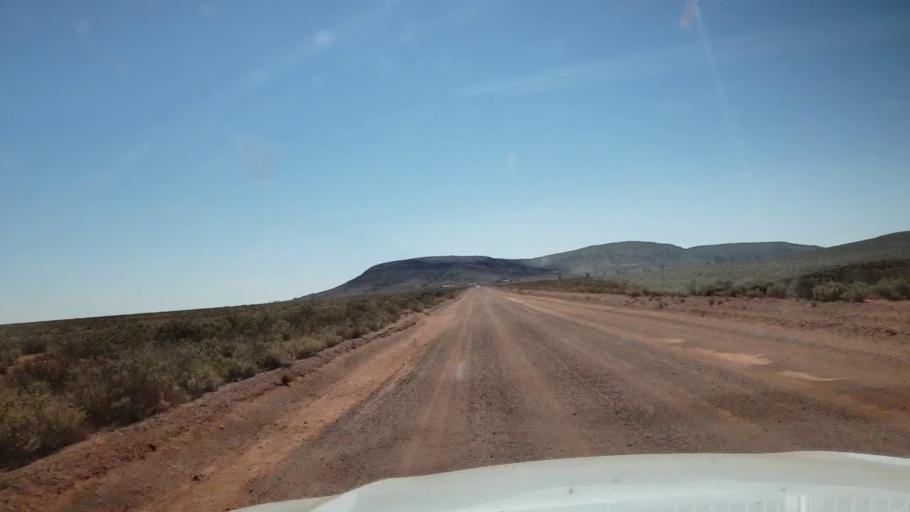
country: AU
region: South Australia
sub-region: Whyalla
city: Whyalla
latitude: -32.7029
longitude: 137.1357
